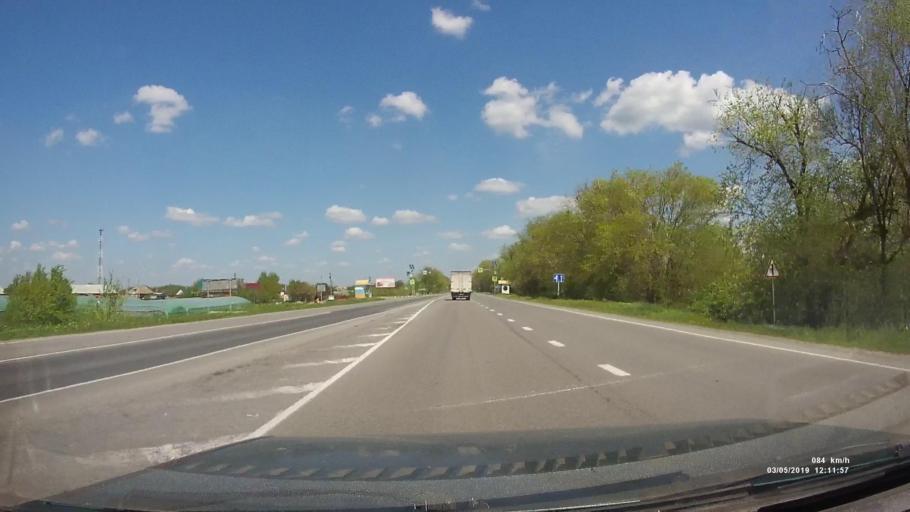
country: RU
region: Rostov
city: Bagayevskaya
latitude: 47.3160
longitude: 40.5425
